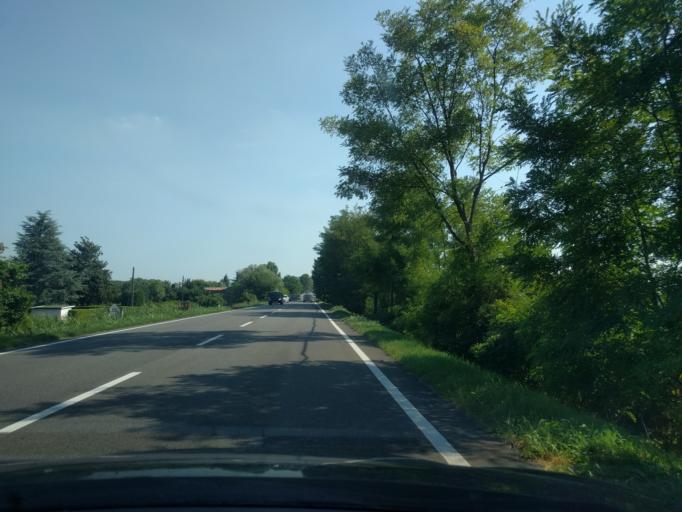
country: IT
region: Veneto
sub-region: Provincia di Padova
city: Stanghella
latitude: 45.1504
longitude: 11.7568
